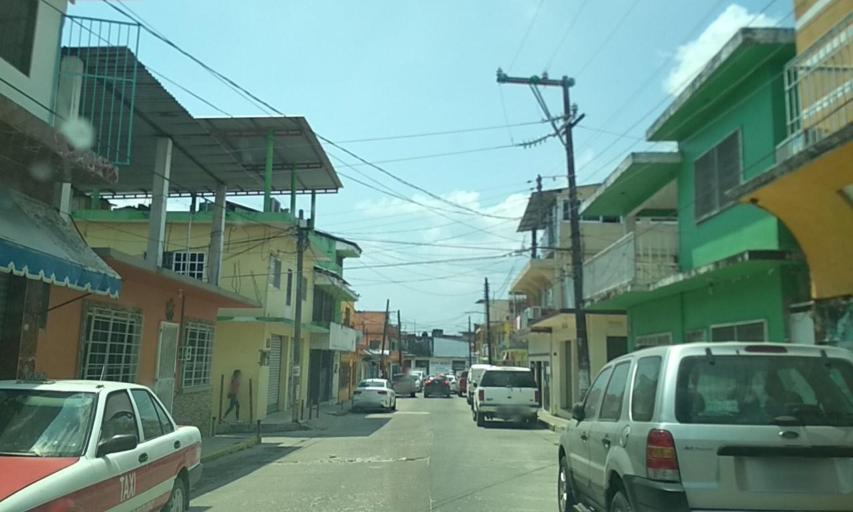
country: MX
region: Veracruz
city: Las Choapas
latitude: 17.9110
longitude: -94.0897
